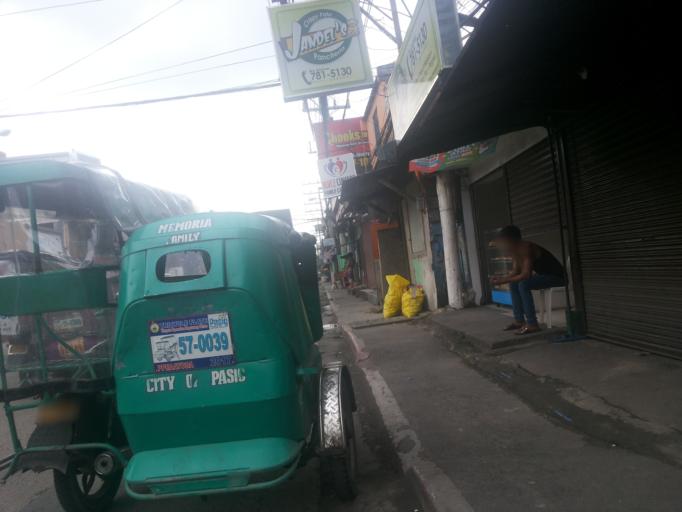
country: PH
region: Calabarzon
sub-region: Province of Rizal
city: Pateros
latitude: 14.5560
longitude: 121.0887
